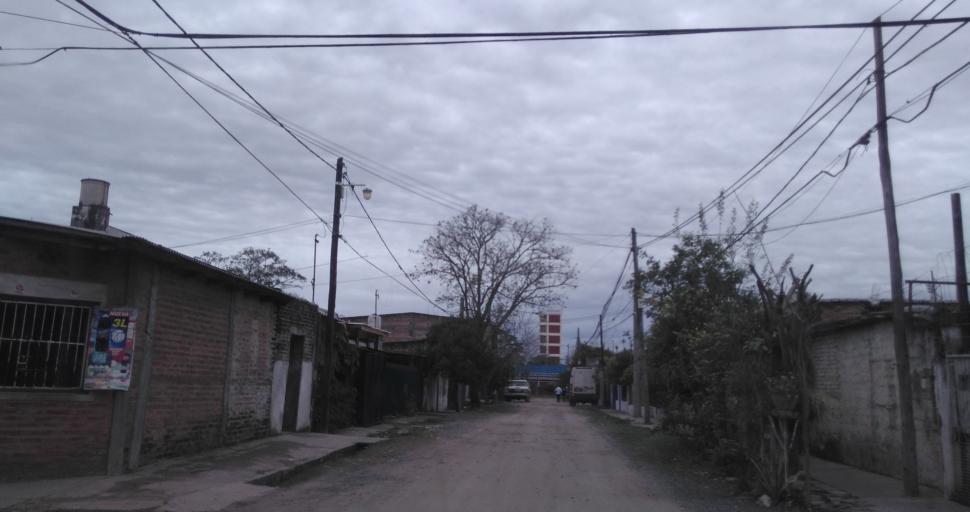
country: AR
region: Chaco
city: Resistencia
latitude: -27.4676
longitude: -58.9689
